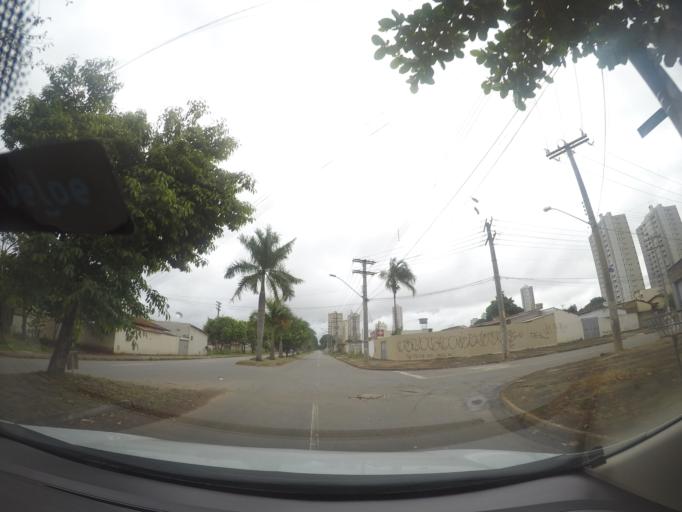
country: BR
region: Goias
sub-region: Goiania
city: Goiania
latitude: -16.7280
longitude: -49.2892
